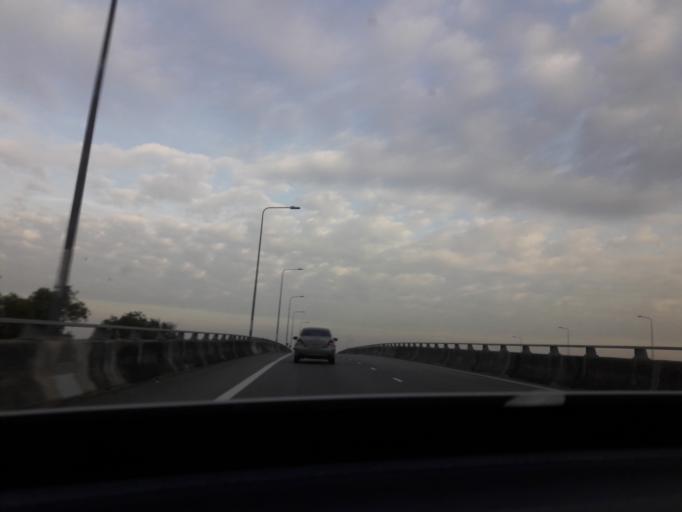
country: TH
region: Phra Nakhon Si Ayutthaya
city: Bang Pa-in
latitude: 14.1480
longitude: 100.5542
